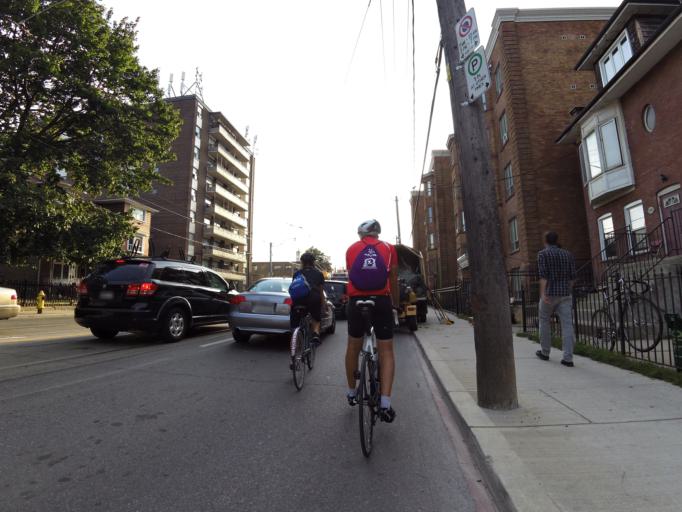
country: CA
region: Ontario
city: Toronto
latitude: 43.6374
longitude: -79.4352
